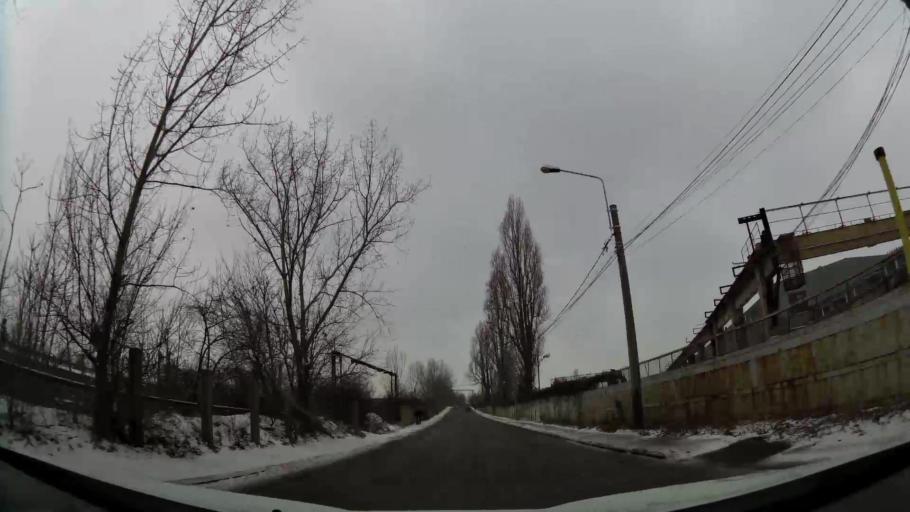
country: RO
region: Prahova
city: Ploiesti
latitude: 44.9234
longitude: 26.0203
